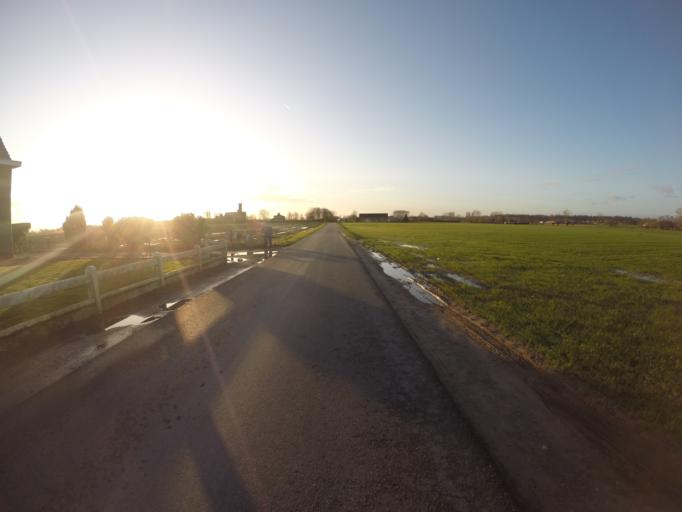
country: BE
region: Flanders
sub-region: Provincie Oost-Vlaanderen
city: Aalter
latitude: 51.0371
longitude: 3.4756
